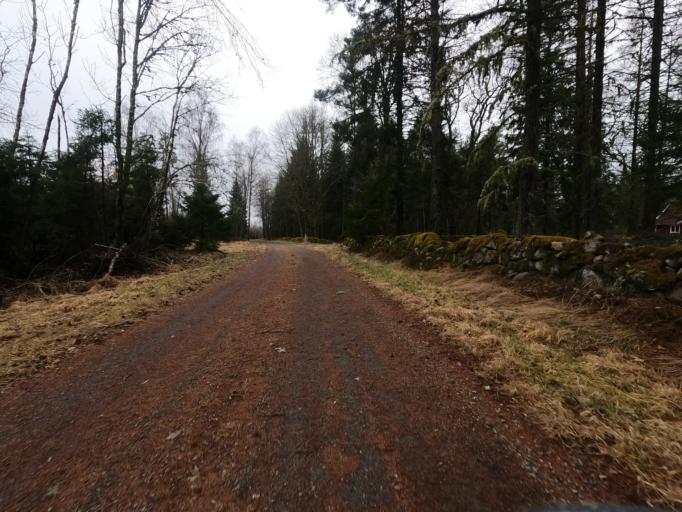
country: SE
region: Kronoberg
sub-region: Markaryds Kommun
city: Stromsnasbruk
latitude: 56.8025
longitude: 13.5641
